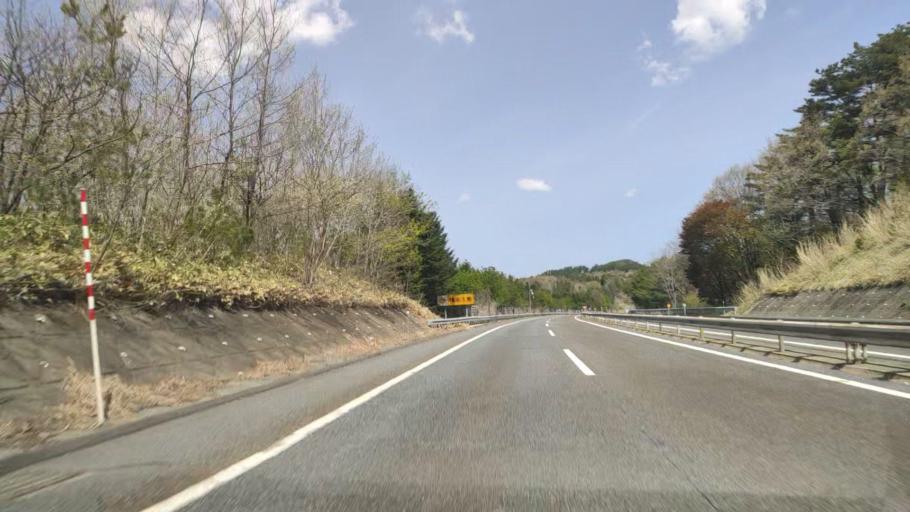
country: JP
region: Aomori
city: Hachinohe
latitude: 40.3486
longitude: 141.4479
